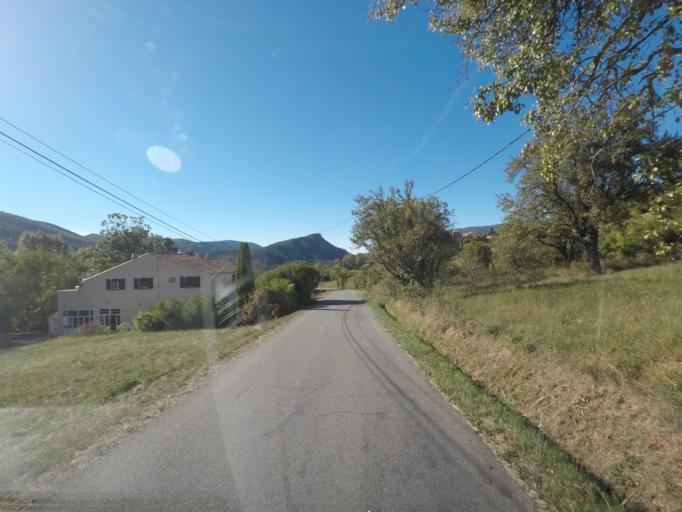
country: FR
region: Provence-Alpes-Cote d'Azur
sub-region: Departement des Hautes-Alpes
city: Serres
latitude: 44.4487
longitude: 5.5473
